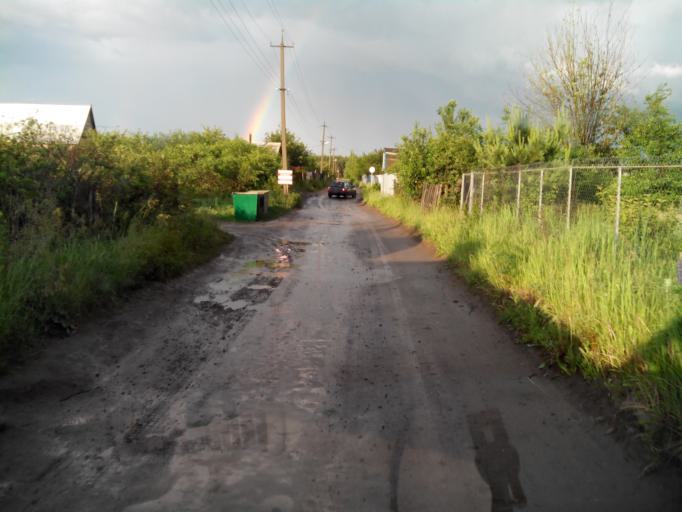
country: RU
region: Penza
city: Zasechnoye
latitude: 53.0388
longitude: 45.0473
